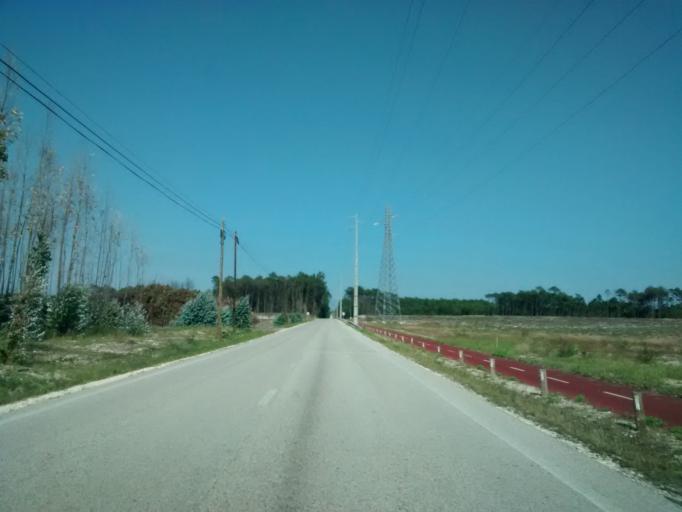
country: PT
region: Leiria
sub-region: Leiria
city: Monte Redondo
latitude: 39.9797
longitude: -8.8450
